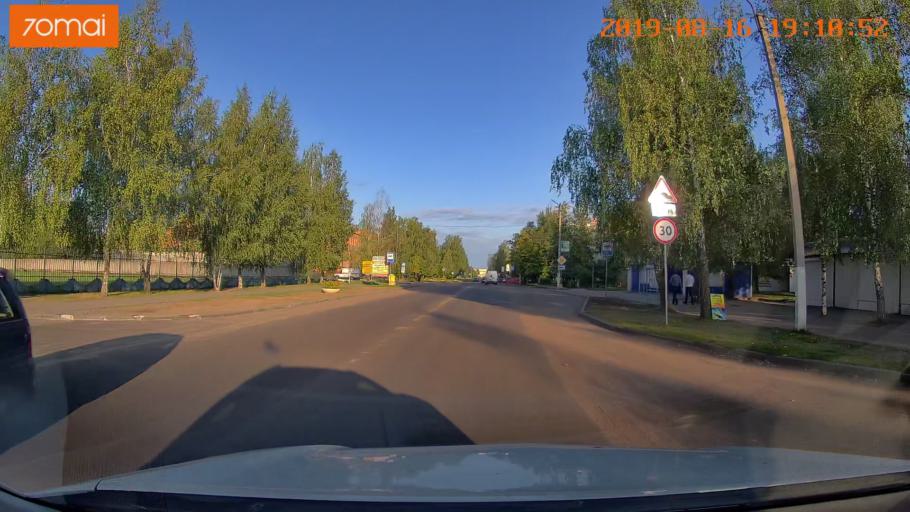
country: BY
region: Mogilev
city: Asipovichy
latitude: 53.3227
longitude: 28.6444
